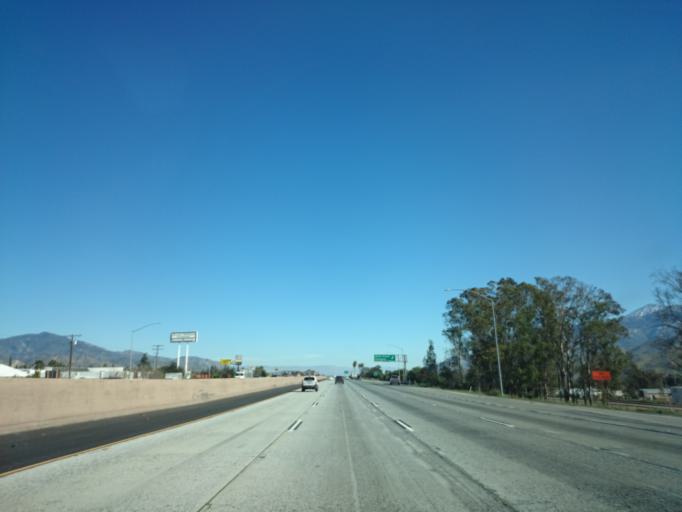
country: US
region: California
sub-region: Riverside County
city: Banning
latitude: 33.9242
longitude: -116.9070
